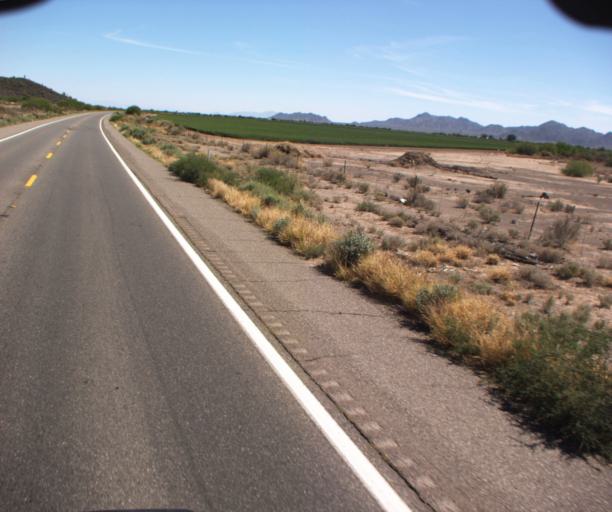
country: US
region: Arizona
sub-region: Pinal County
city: Sacaton
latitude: 33.1157
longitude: -111.7252
